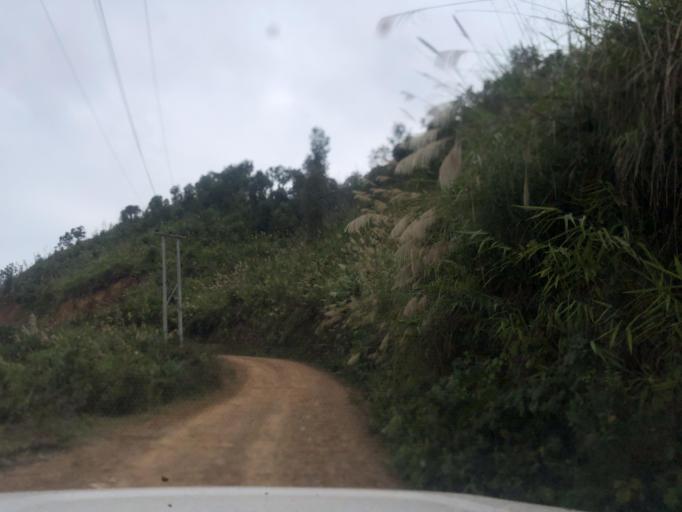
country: LA
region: Phongsali
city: Khoa
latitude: 21.2541
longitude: 102.5894
